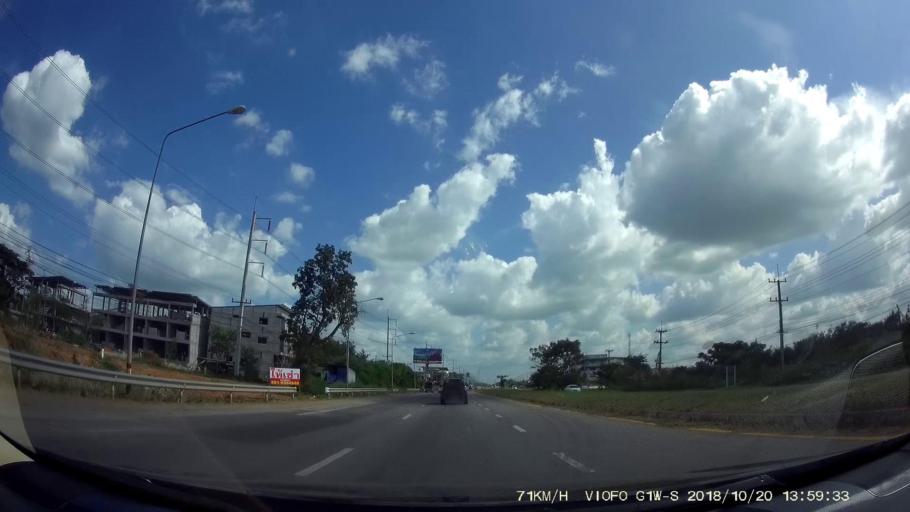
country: TH
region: Khon Kaen
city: Chum Phae
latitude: 16.5236
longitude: 102.1134
